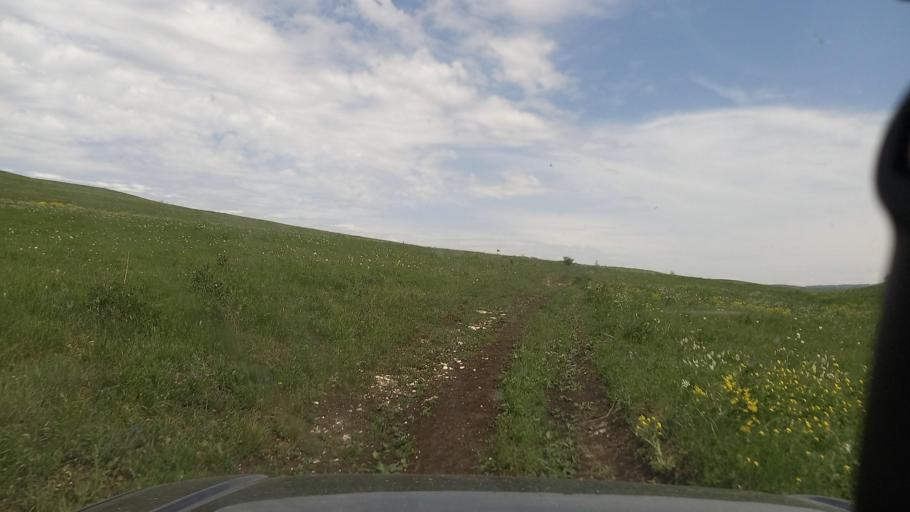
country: RU
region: Karachayevo-Cherkesiya
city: Pregradnaya
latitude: 44.0700
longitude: 41.2897
